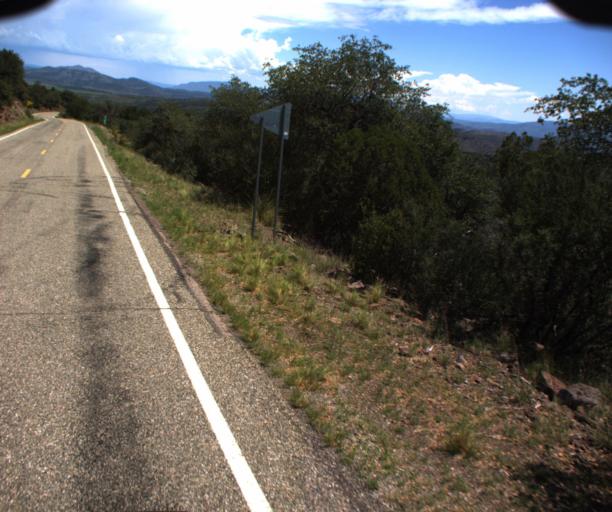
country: US
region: Arizona
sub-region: Greenlee County
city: Morenci
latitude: 33.2531
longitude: -109.3708
